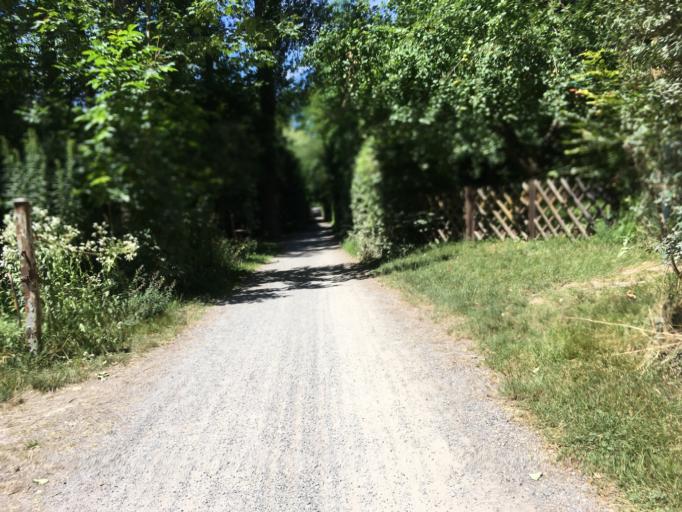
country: DE
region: Baden-Wuerttemberg
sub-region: Regierungsbezirk Stuttgart
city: Oberriexingen
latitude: 48.9264
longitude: 9.0103
